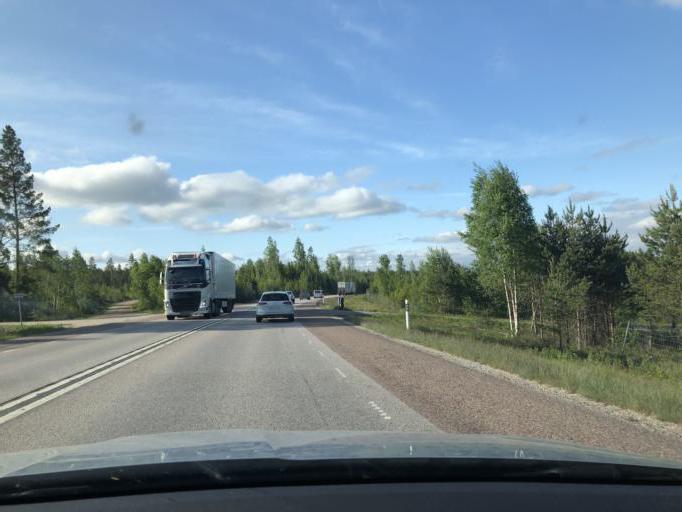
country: SE
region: Gaevleborg
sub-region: Nordanstigs Kommun
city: Bergsjoe
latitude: 62.0055
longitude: 17.2364
